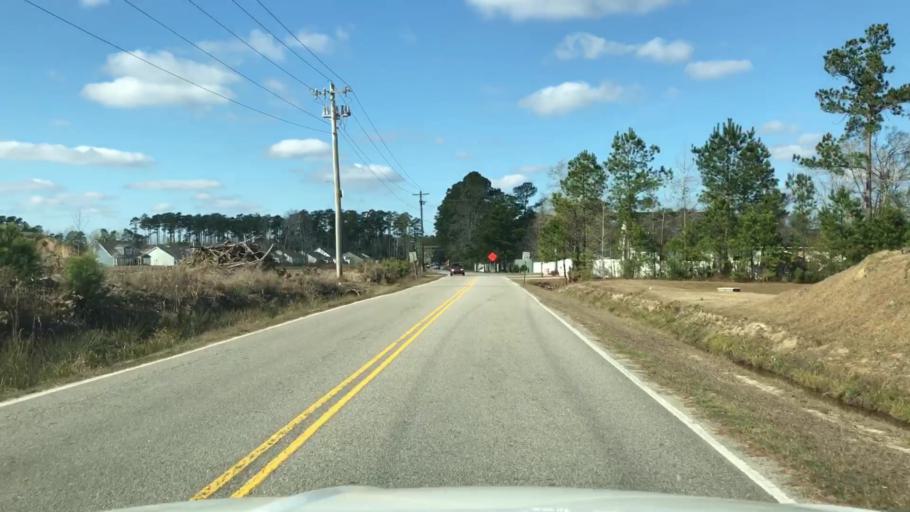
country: US
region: South Carolina
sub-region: Horry County
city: Socastee
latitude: 33.6592
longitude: -79.0062
